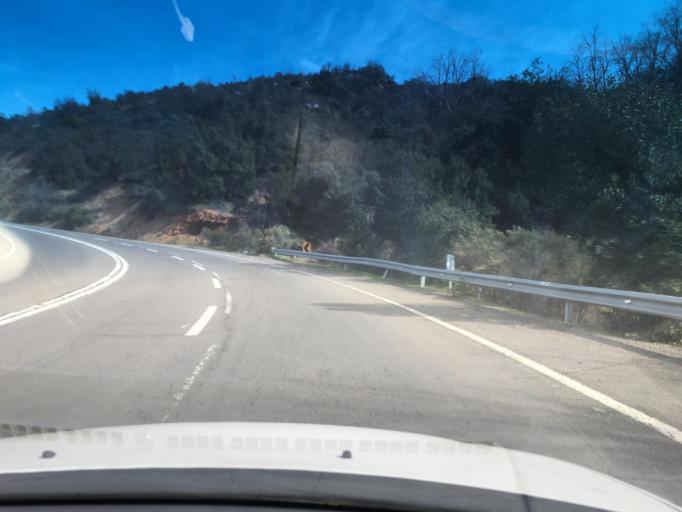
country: CL
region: Valparaiso
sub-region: Provincia de San Felipe
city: Llaillay
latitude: -33.0567
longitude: -71.0036
